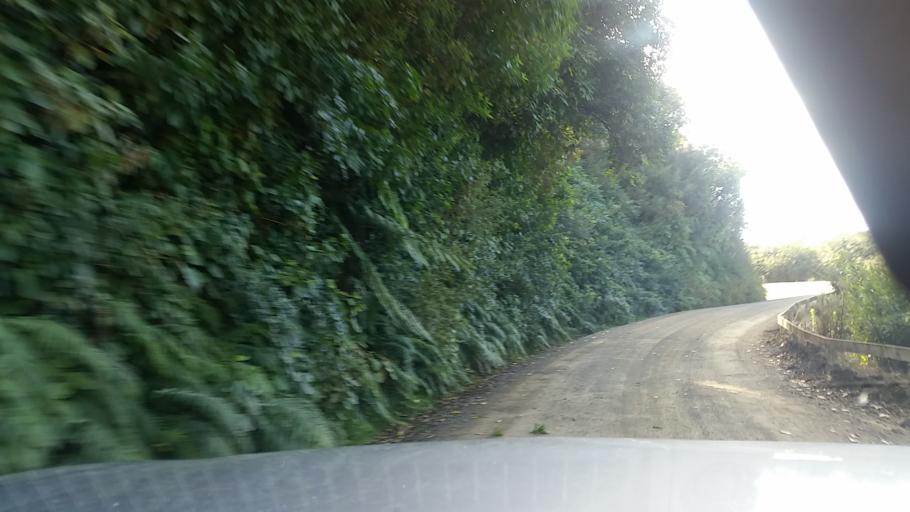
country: NZ
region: Marlborough
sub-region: Marlborough District
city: Picton
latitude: -41.2949
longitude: 174.1239
